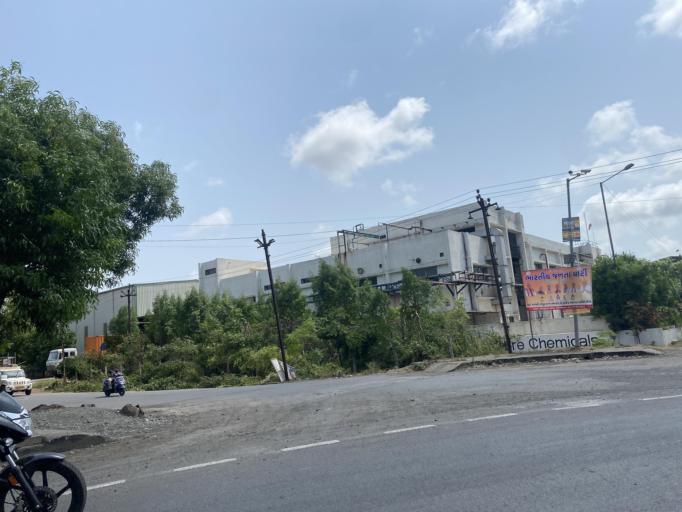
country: IN
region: Gujarat
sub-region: Valsad
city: Vapi
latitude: 20.2853
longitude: 72.8516
